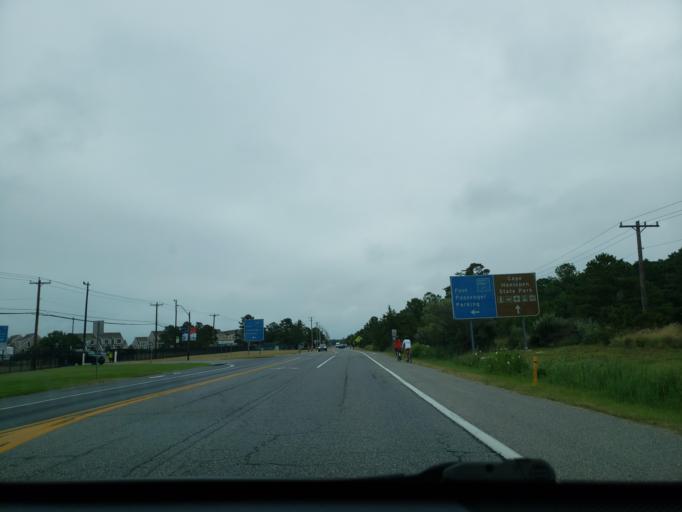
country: US
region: Delaware
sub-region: Sussex County
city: Lewes
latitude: 38.7801
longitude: -75.1193
